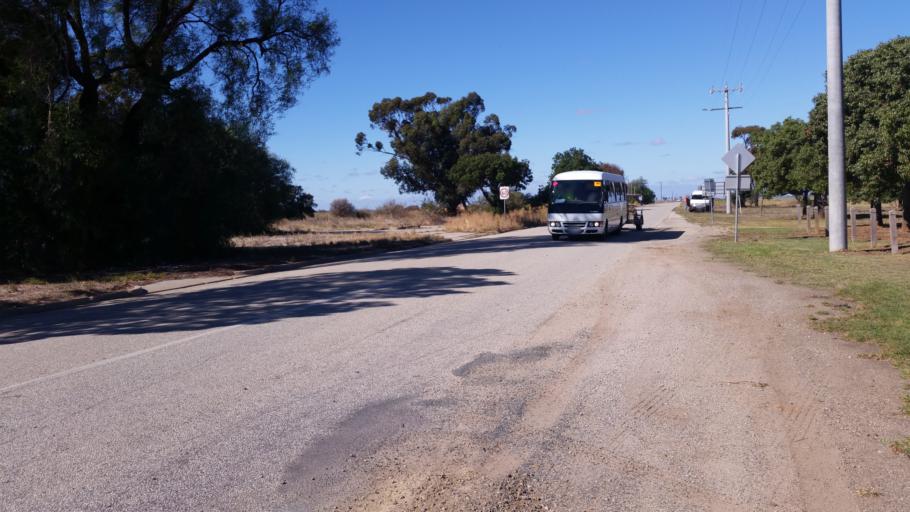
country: AU
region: Victoria
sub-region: Greater Bendigo
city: Epsom
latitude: -36.2114
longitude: 144.2319
